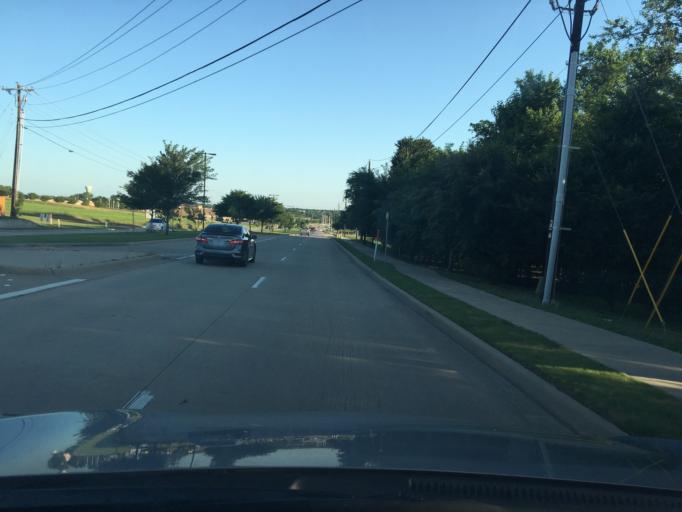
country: US
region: Texas
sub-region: Collin County
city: McKinney
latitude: 33.2226
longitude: -96.6792
